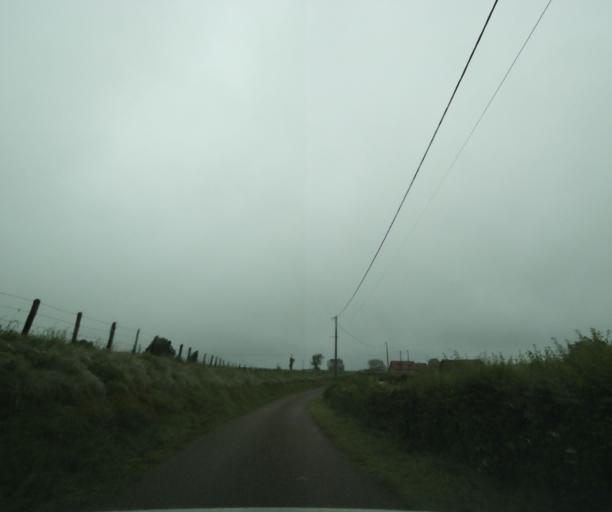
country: FR
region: Bourgogne
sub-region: Departement de Saone-et-Loire
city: Charolles
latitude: 46.4031
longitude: 4.3866
